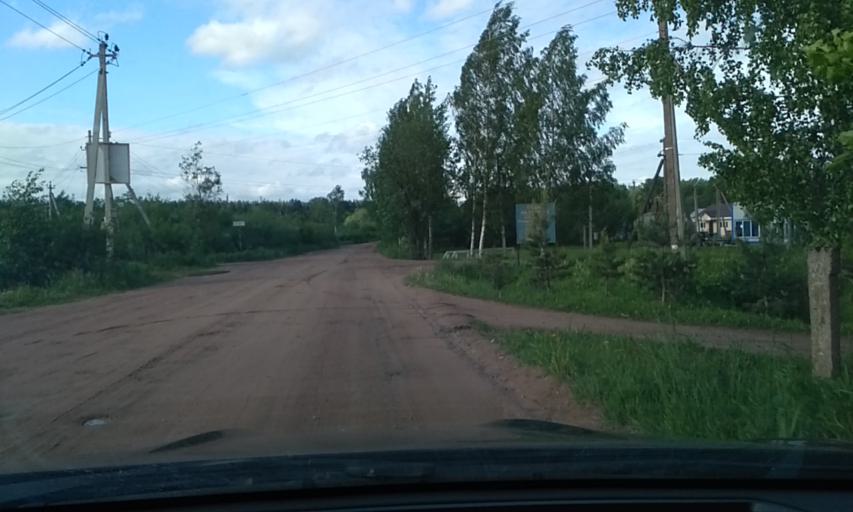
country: RU
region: Leningrad
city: Otradnoye
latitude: 59.8043
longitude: 30.8051
